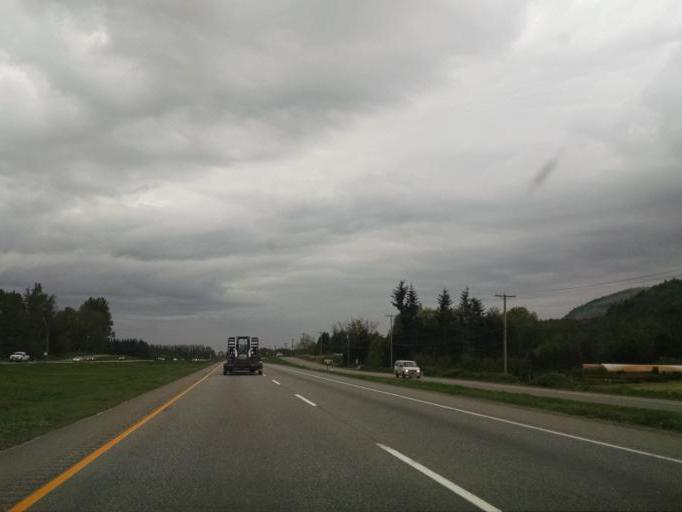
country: CA
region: British Columbia
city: Abbotsford
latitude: 49.0706
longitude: -122.1561
